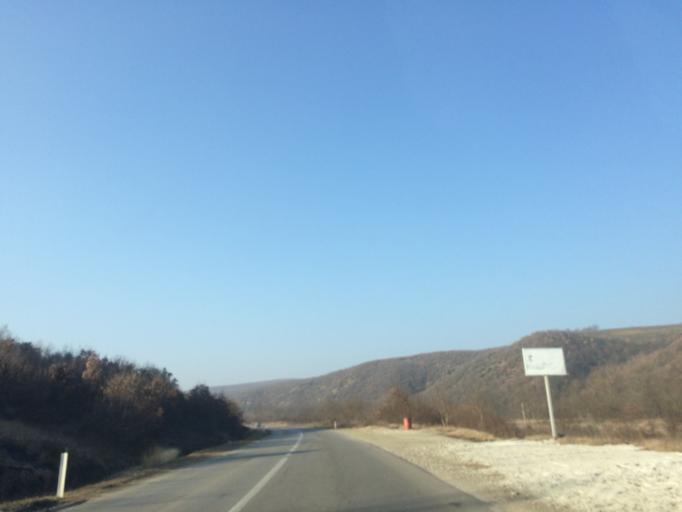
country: XK
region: Pec
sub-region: Komuna e Pejes
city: Kosuriq
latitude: 42.5068
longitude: 20.5303
